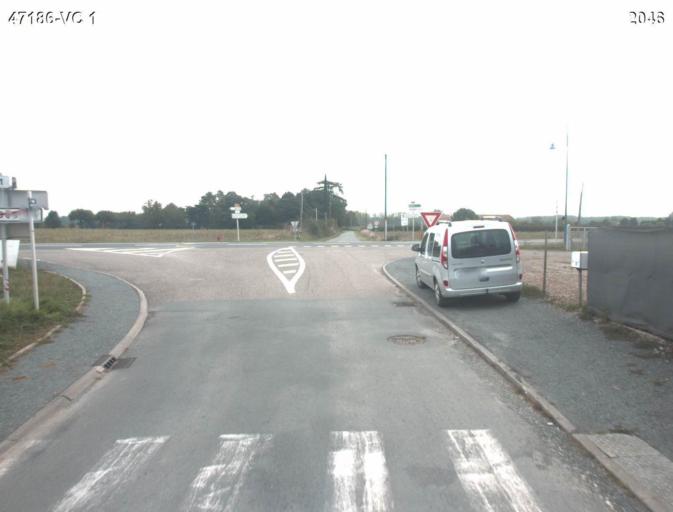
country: FR
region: Aquitaine
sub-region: Departement du Lot-et-Garonne
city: Port-Sainte-Marie
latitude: 44.2054
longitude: 0.4383
